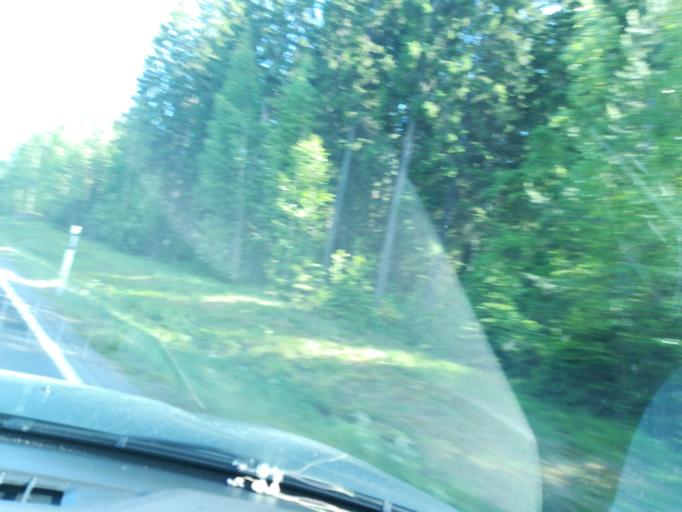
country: FI
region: Southern Savonia
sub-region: Mikkeli
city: Puumala
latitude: 61.5099
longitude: 28.1836
